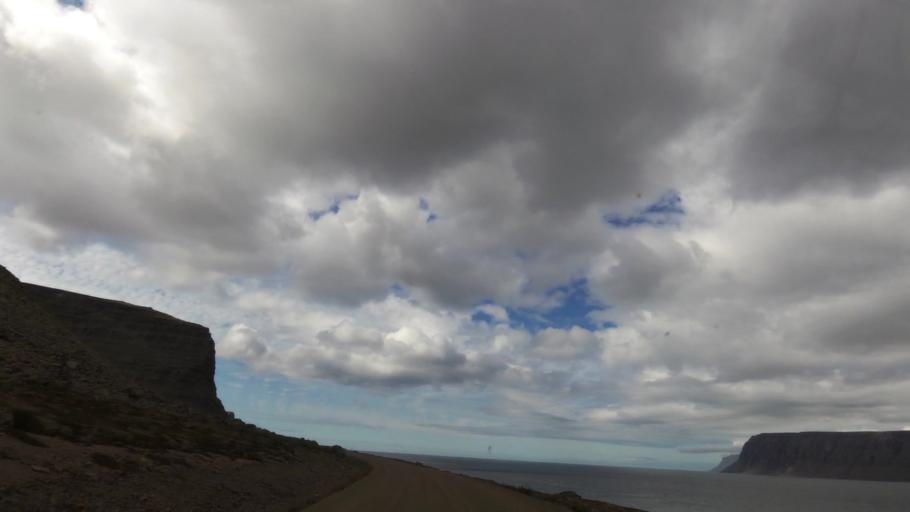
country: IS
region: West
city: Olafsvik
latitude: 65.5753
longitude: -24.0664
